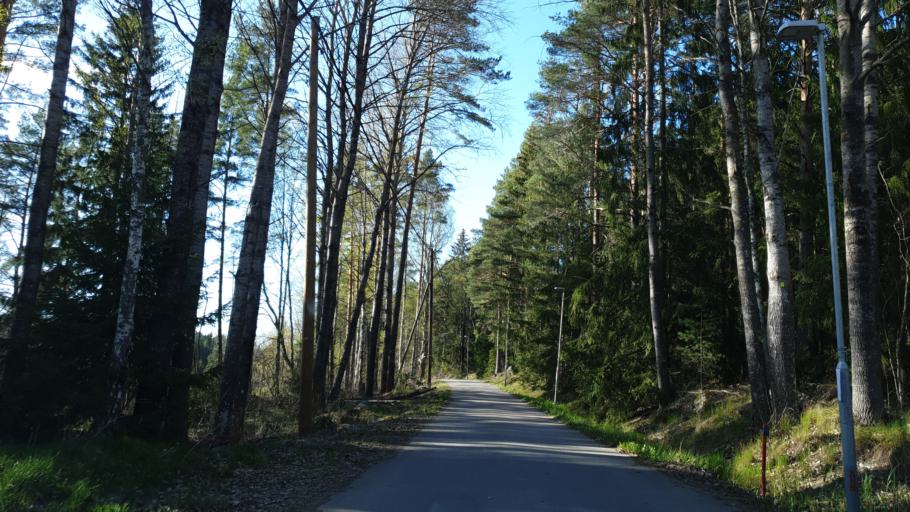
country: SE
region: Stockholm
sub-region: Upplands Vasby Kommun
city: Upplands Vaesby
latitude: 59.5181
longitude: 17.8760
